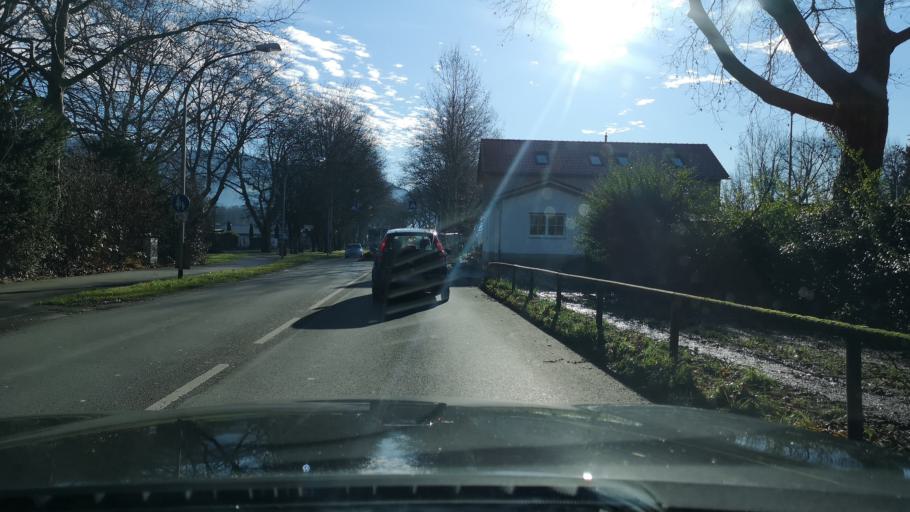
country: AT
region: Vorarlberg
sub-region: Politischer Bezirk Bregenz
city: Horbranz
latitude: 47.5425
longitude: 9.7283
